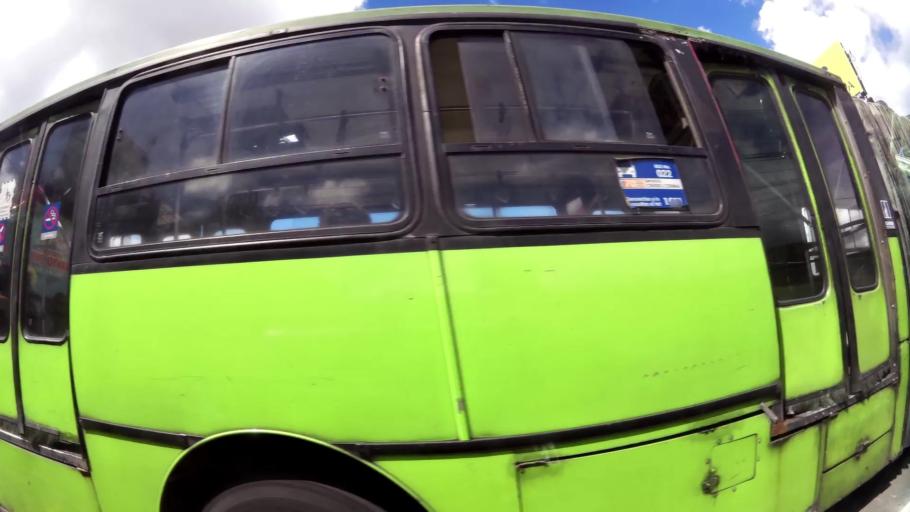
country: GT
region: Guatemala
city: Guatemala City
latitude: 14.6064
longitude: -90.5432
